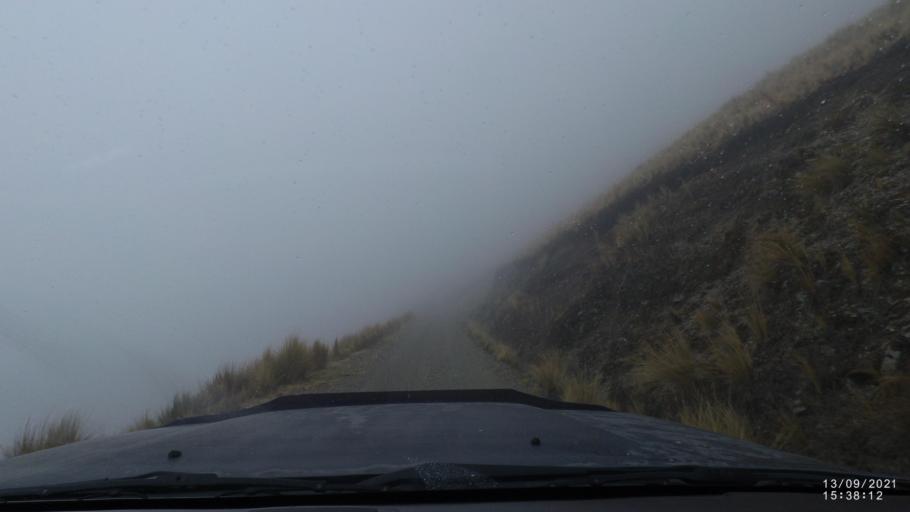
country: BO
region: Cochabamba
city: Colomi
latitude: -17.3284
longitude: -65.7238
